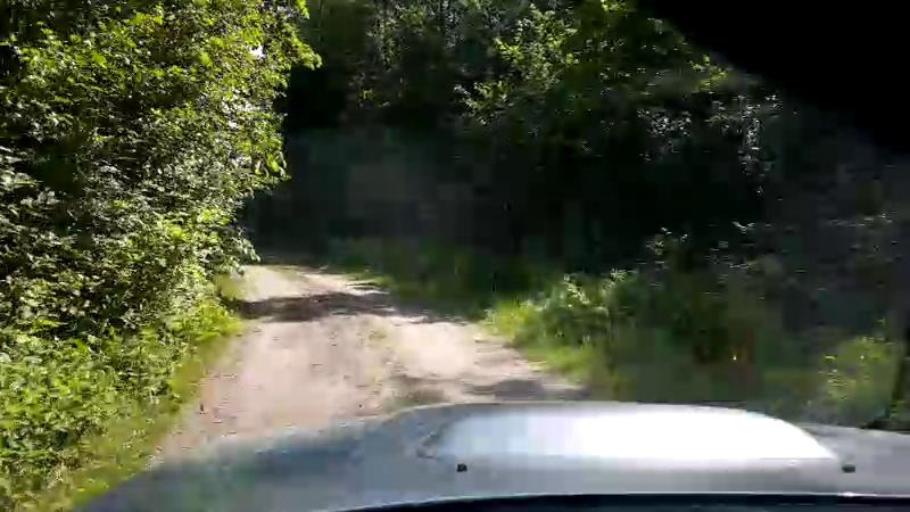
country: EE
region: Paernumaa
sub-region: Sindi linn
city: Sindi
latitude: 58.5329
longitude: 24.6564
